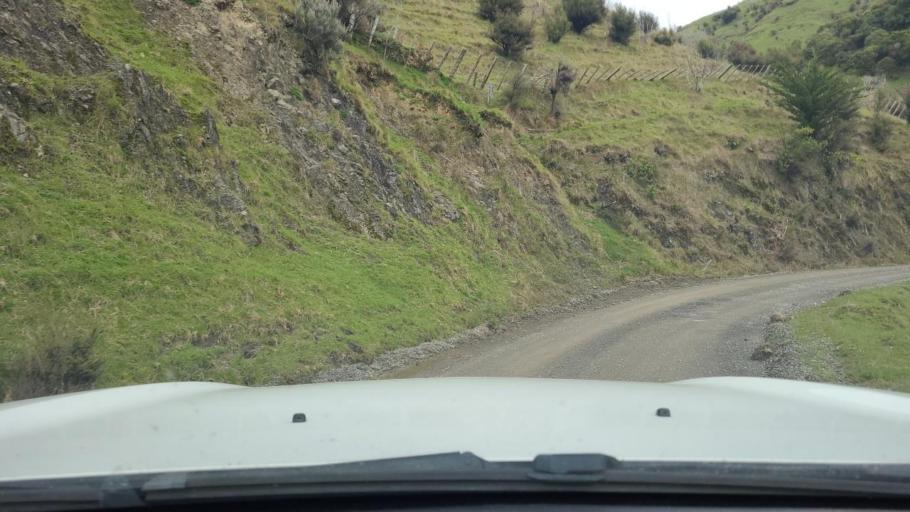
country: NZ
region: Wellington
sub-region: South Wairarapa District
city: Waipawa
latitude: -41.3666
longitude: 175.3944
